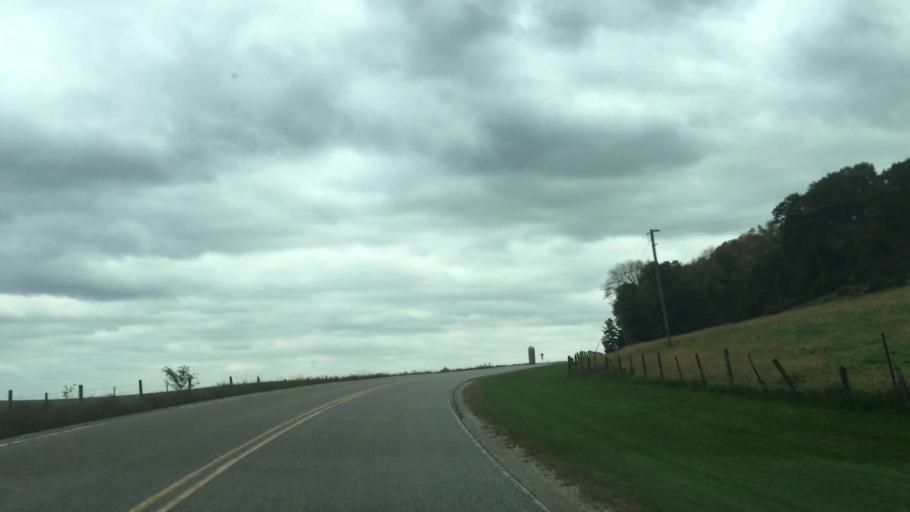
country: US
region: Minnesota
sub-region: Fillmore County
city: Preston
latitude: 43.7415
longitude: -92.0115
